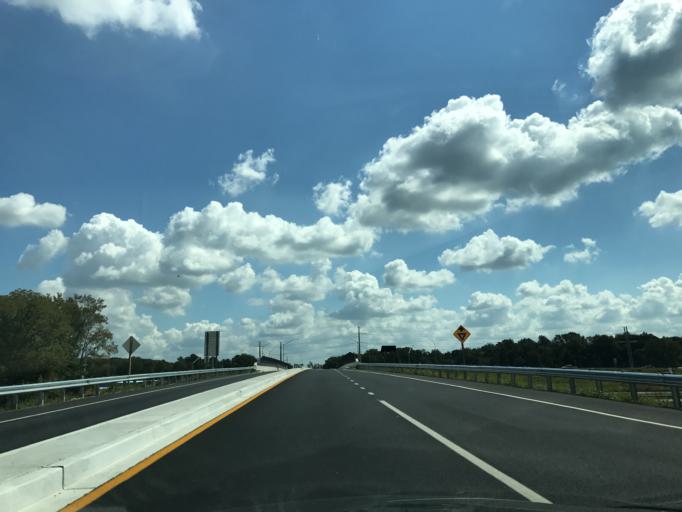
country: US
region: Maryland
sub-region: Queen Anne's County
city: Centreville
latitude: 39.0279
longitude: -76.0284
